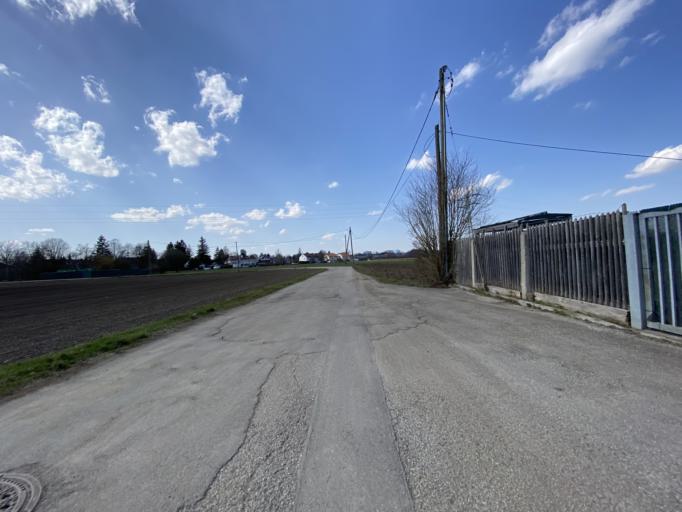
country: DE
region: Bavaria
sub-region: Upper Bavaria
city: Unterfoehring
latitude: 48.1584
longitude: 11.6552
